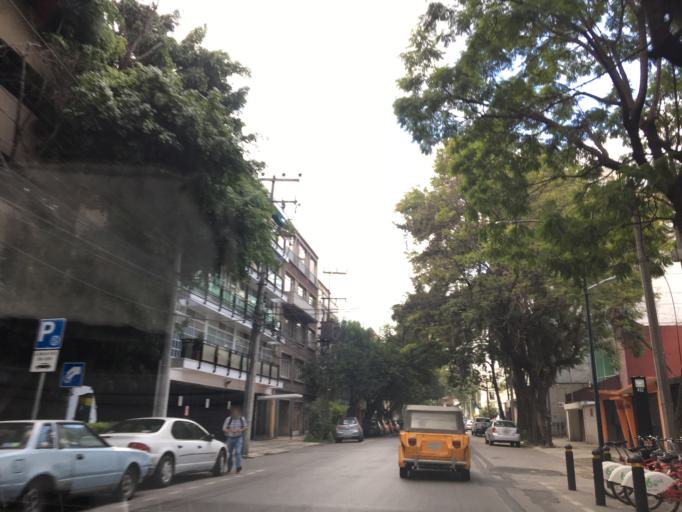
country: MX
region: Mexico City
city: Miguel Hidalgo
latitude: 19.4360
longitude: -99.1798
